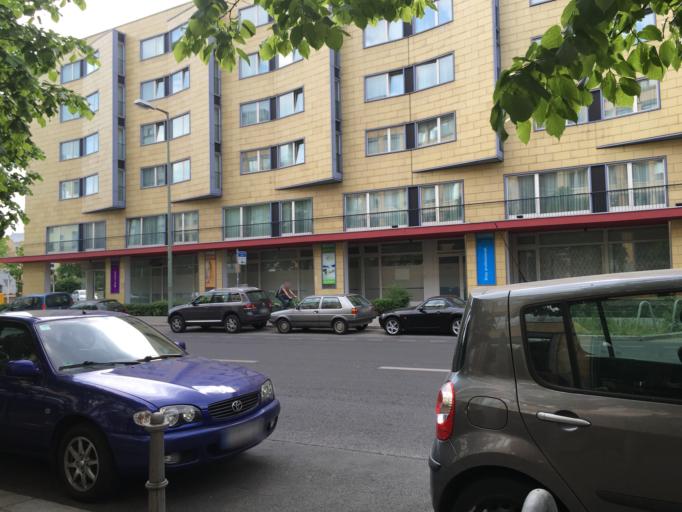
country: DE
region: Berlin
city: Hansaviertel
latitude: 52.5035
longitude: 13.3528
